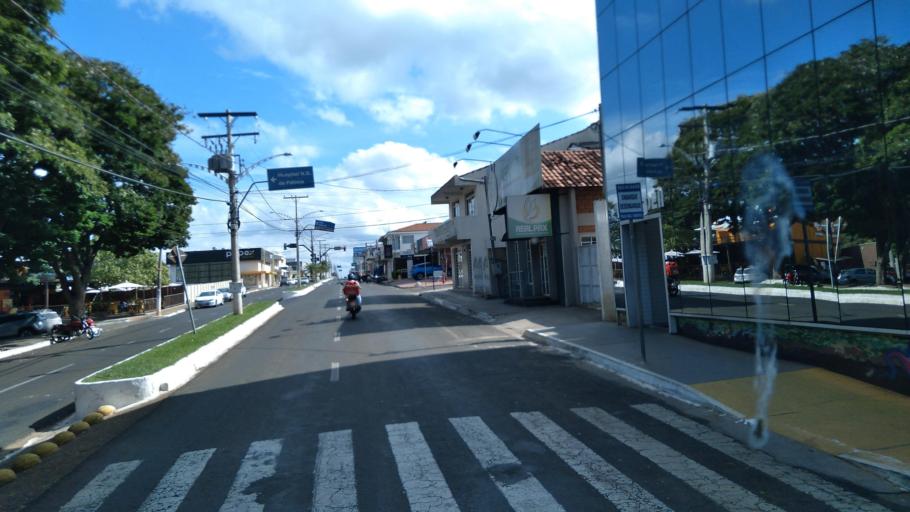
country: BR
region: Goias
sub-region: Mineiros
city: Mineiros
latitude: -17.5642
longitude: -52.5557
